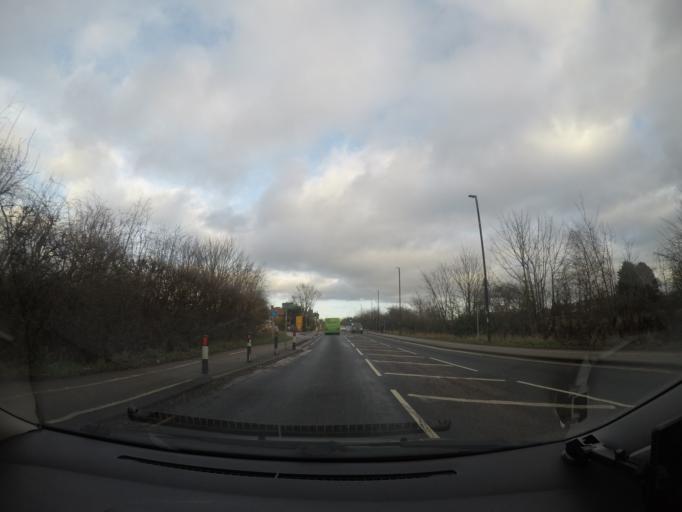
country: GB
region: England
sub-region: City of York
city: Huntington
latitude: 53.9746
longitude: -1.0596
